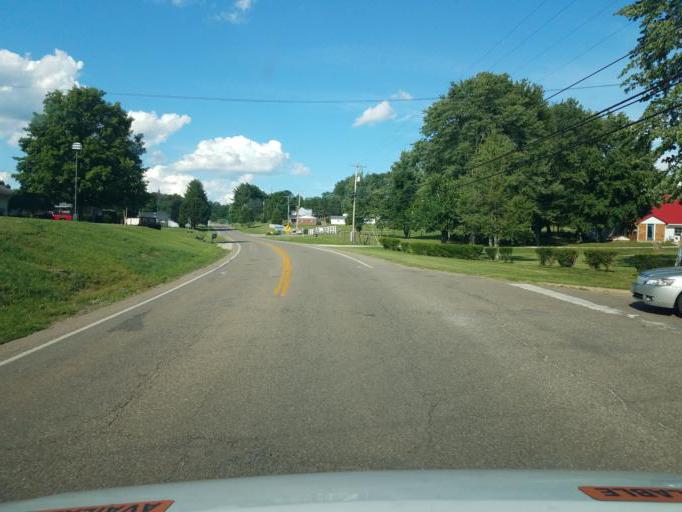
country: US
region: Ohio
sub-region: Gallia County
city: Gallipolis
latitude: 38.7991
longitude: -82.2443
